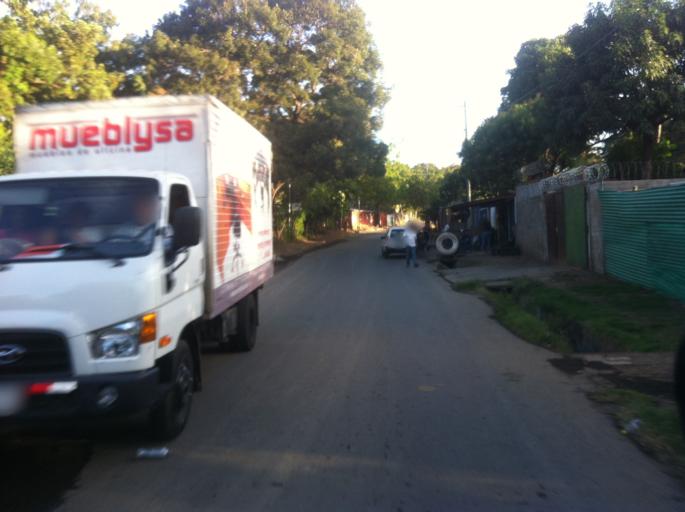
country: NI
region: Managua
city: Ciudad Sandino
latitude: 12.1070
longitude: -86.3101
